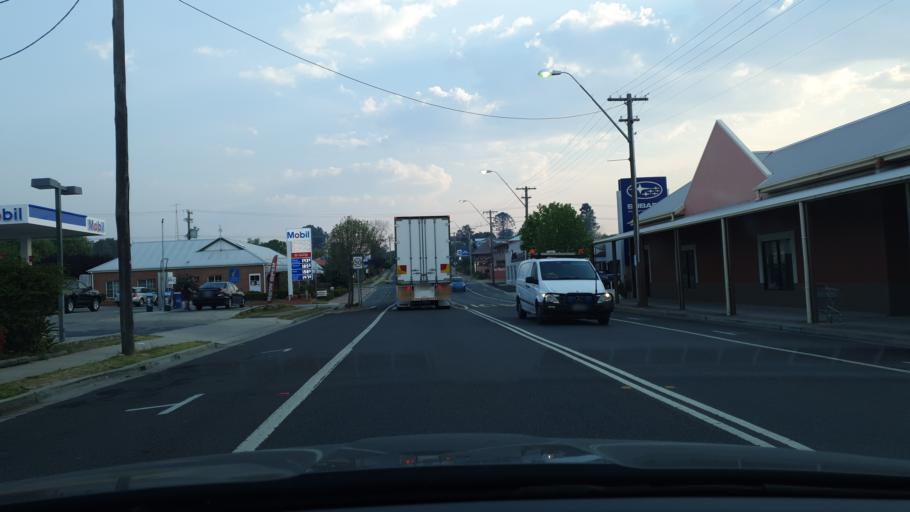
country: AU
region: New South Wales
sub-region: Tenterfield Municipality
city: Carrolls Creek
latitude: -29.0565
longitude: 152.0186
